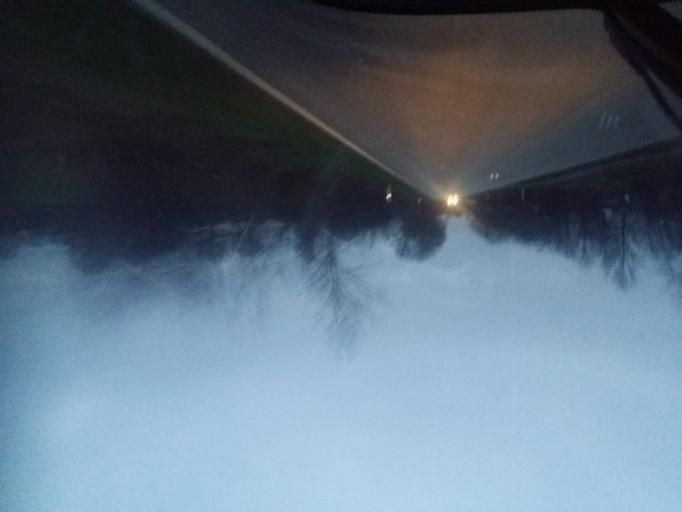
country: DE
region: Schleswig-Holstein
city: Schenefeld
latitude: 54.0598
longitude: 9.4759
